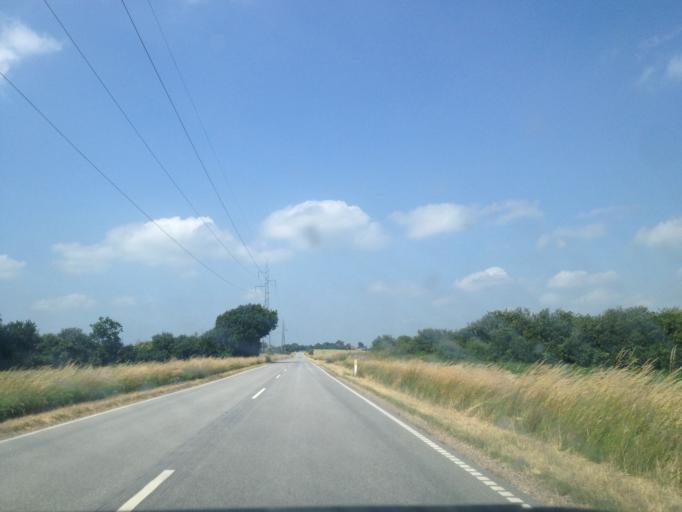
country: DK
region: South Denmark
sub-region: Kolding Kommune
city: Vamdrup
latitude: 55.3669
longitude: 9.2821
